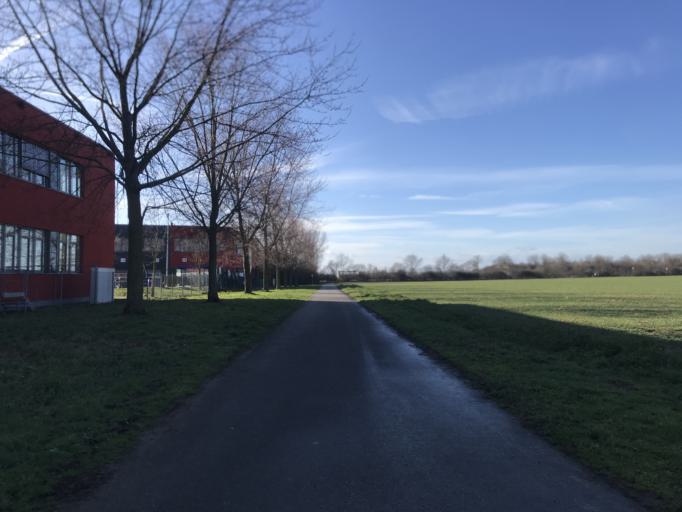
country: DE
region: Hesse
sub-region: Regierungsbezirk Darmstadt
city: Hochheim am Main
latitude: 50.0576
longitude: 8.3274
